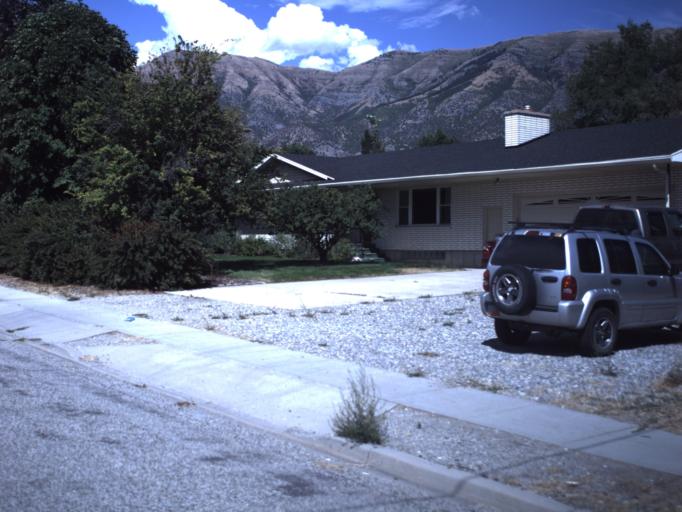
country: US
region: Utah
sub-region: Box Elder County
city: Honeyville
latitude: 41.6393
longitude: -112.0796
